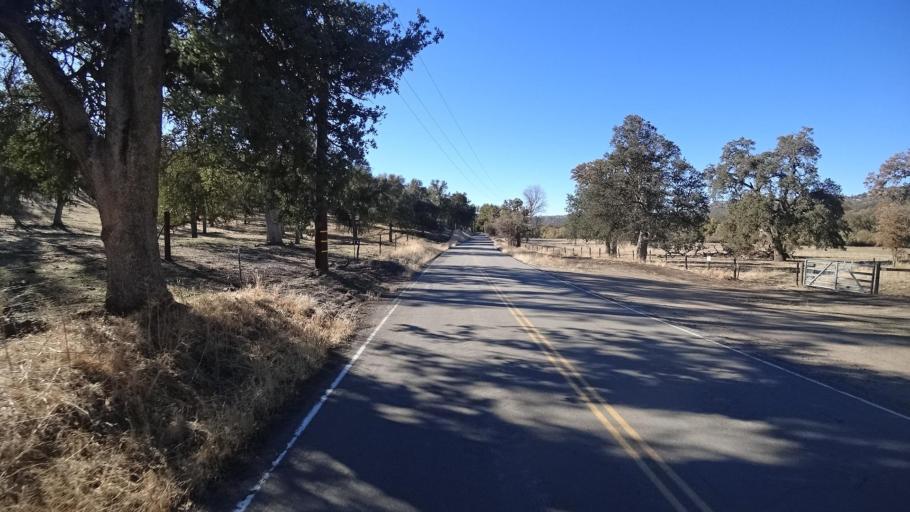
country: US
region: California
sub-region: Kern County
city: Alta Sierra
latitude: 35.7408
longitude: -118.7164
